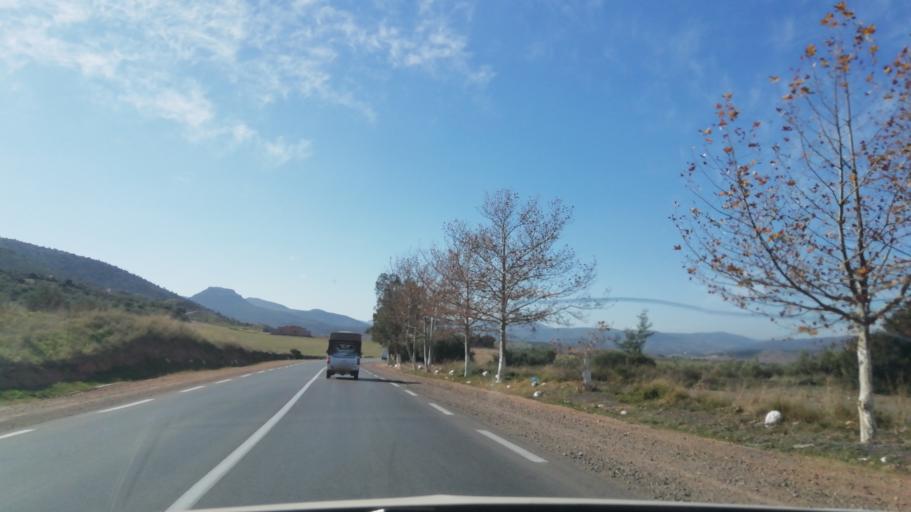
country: DZ
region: Tlemcen
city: Ouled Mimoun
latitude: 34.8840
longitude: -1.0840
